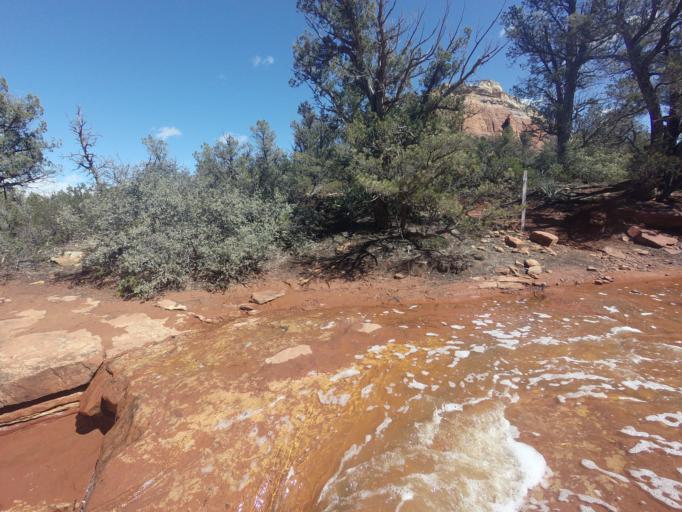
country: US
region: Arizona
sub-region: Yavapai County
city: West Sedona
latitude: 34.9039
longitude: -111.8145
